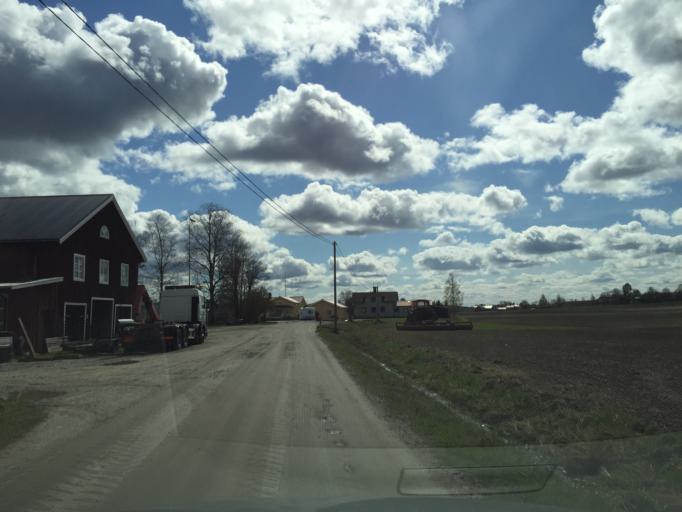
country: SE
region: Gaevleborg
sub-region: Bollnas Kommun
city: Arbra
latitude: 61.5157
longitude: 16.3543
